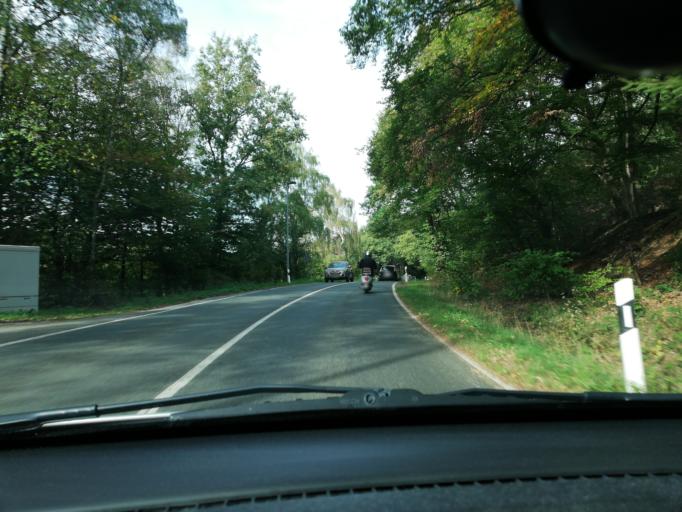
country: DE
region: North Rhine-Westphalia
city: Sprockhovel
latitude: 51.3485
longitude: 7.2526
